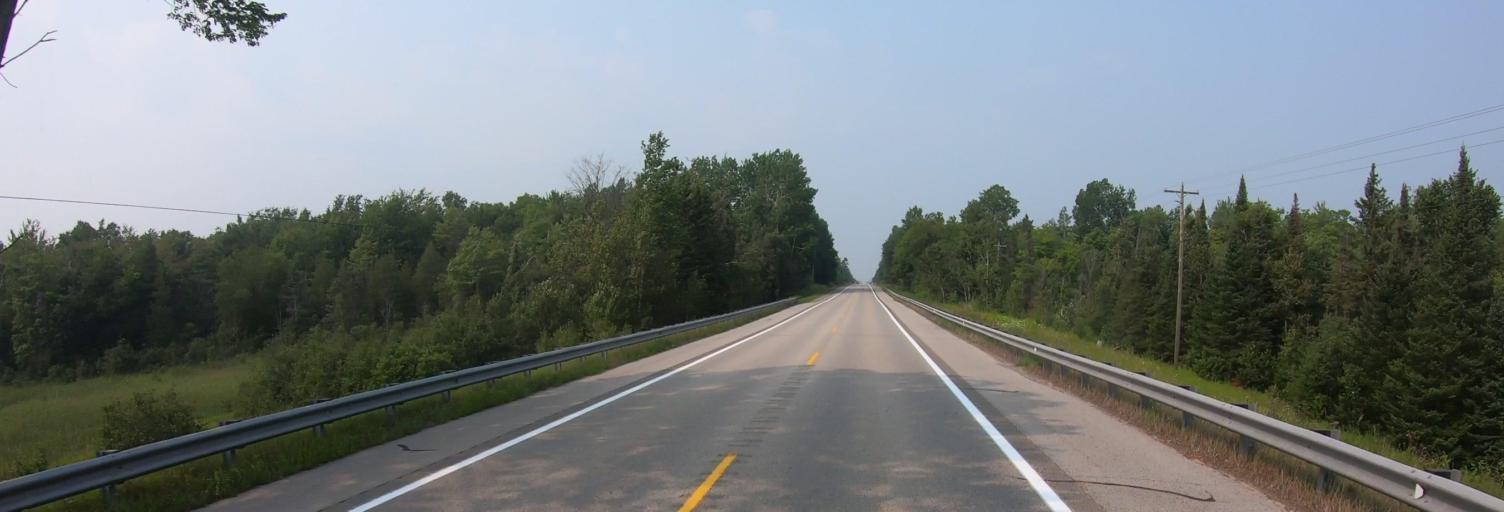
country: US
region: Michigan
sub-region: Chippewa County
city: Sault Ste. Marie
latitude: 46.2487
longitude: -84.3634
